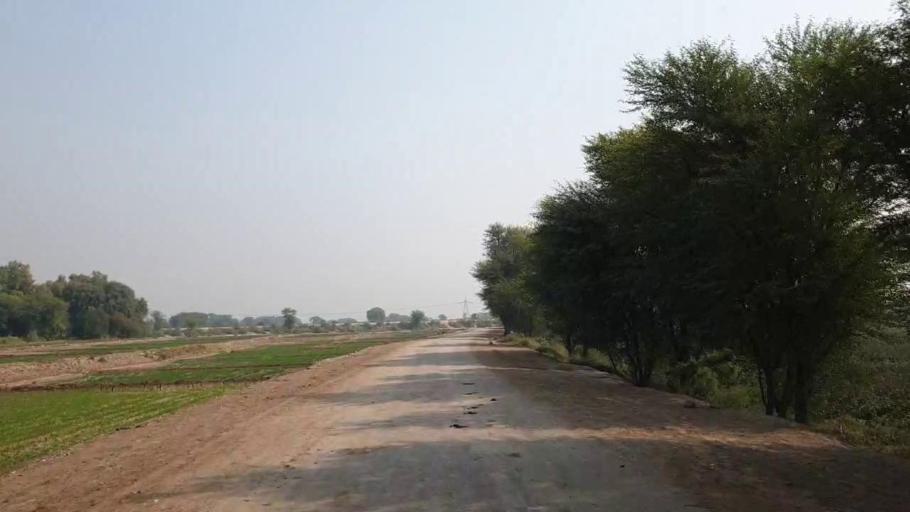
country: PK
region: Sindh
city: Bhan
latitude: 26.5168
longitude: 67.7405
